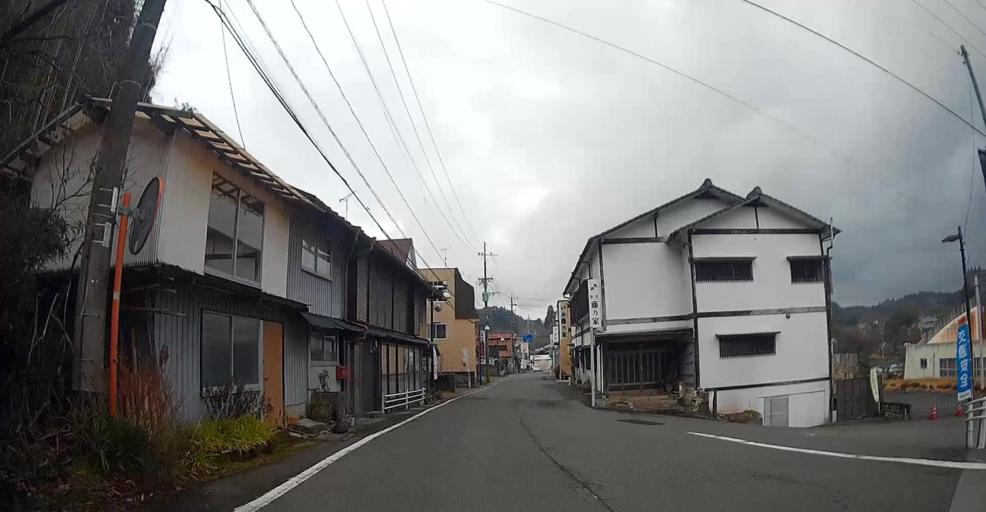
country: JP
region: Kumamoto
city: Ozu
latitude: 32.6818
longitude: 130.9909
